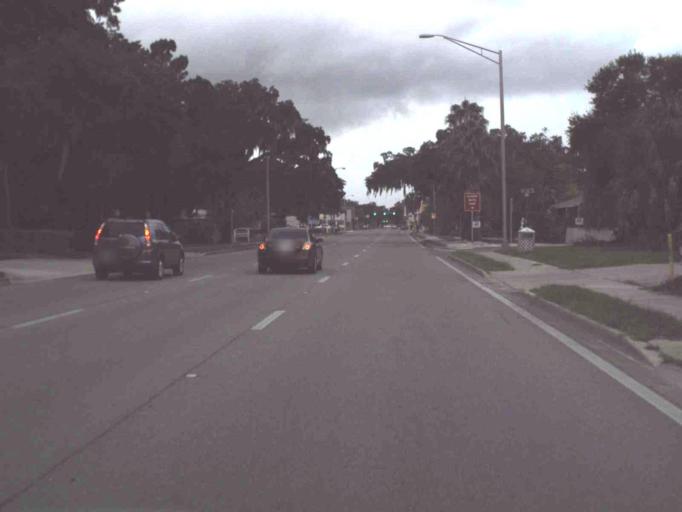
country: US
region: Florida
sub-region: Manatee County
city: Bradenton
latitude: 27.4952
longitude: -82.5511
